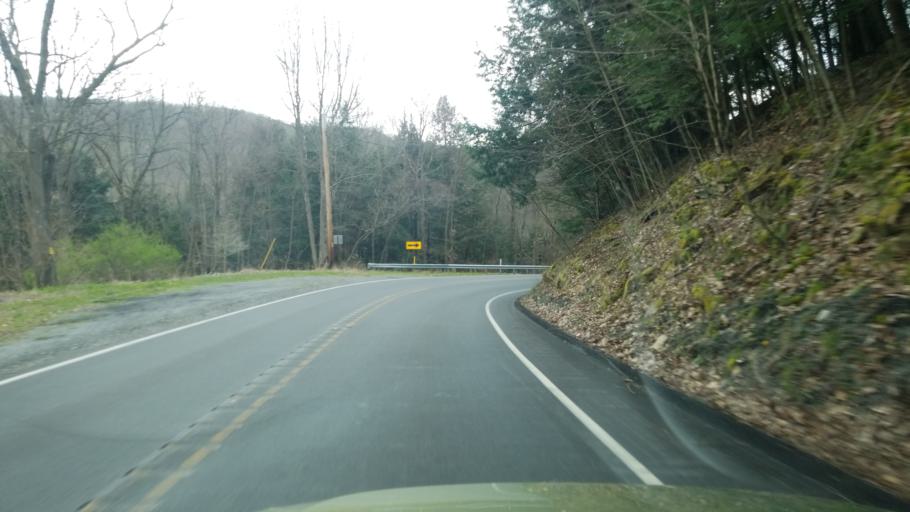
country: US
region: Pennsylvania
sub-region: Clearfield County
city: Curwensville
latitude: 40.8664
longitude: -78.4454
